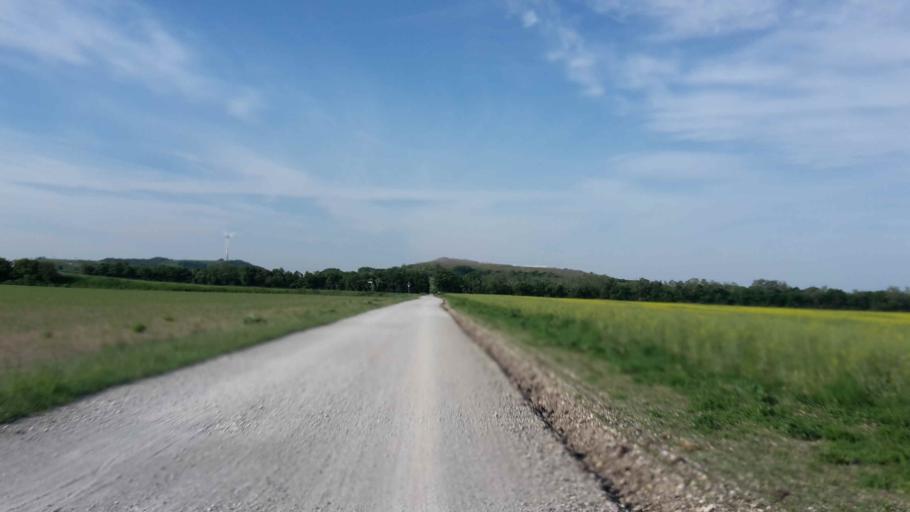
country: DE
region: Bavaria
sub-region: Upper Bavaria
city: Garching bei Munchen
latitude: 48.2352
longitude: 11.6332
